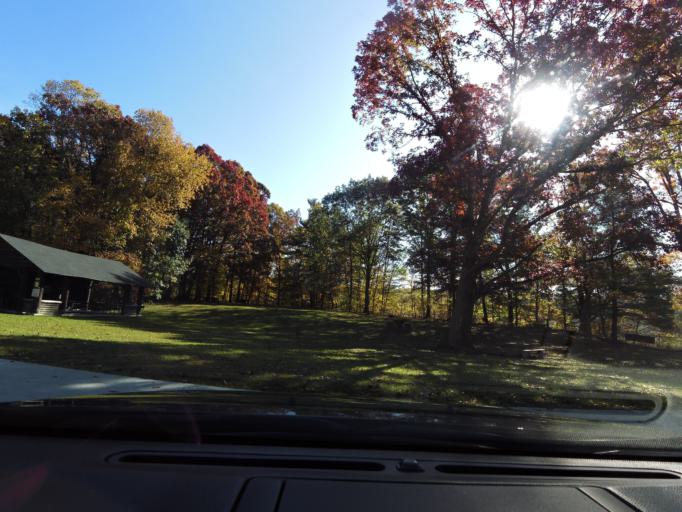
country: US
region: New York
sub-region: Wyoming County
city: Castile
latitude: 42.6170
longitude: -77.9969
